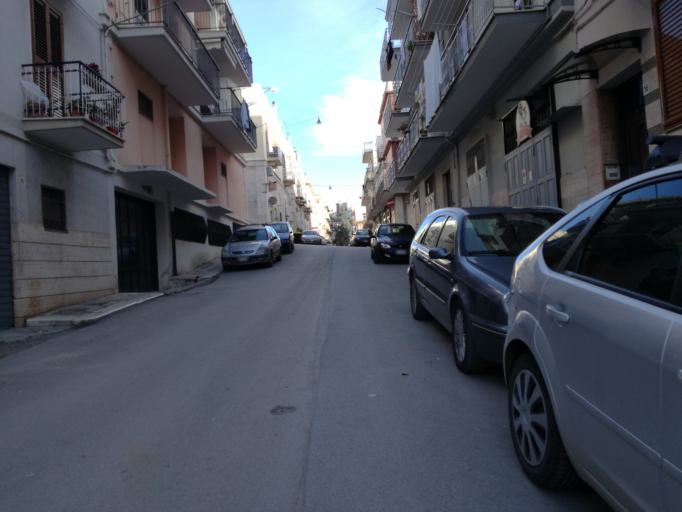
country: IT
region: Apulia
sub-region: Provincia di Bari
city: Ruvo di Puglia
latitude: 41.1146
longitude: 16.4818
